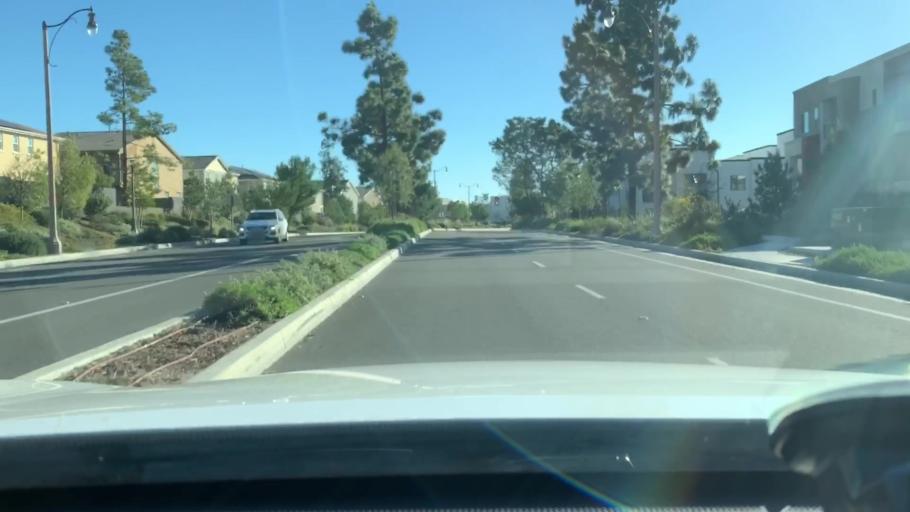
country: US
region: California
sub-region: Orange County
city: Lake Forest
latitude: 33.6874
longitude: -117.7389
